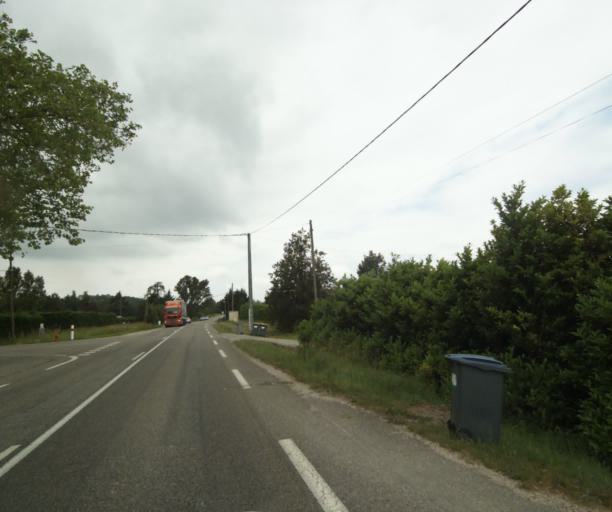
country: FR
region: Midi-Pyrenees
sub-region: Departement du Tarn-et-Garonne
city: Saint-Nauphary
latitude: 43.9774
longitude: 1.4012
